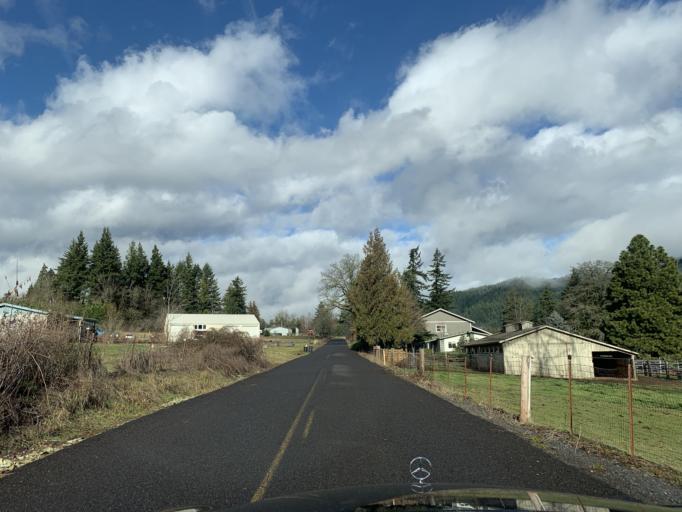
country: US
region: Washington
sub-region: Skamania County
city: Carson
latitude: 45.7228
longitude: -121.8073
